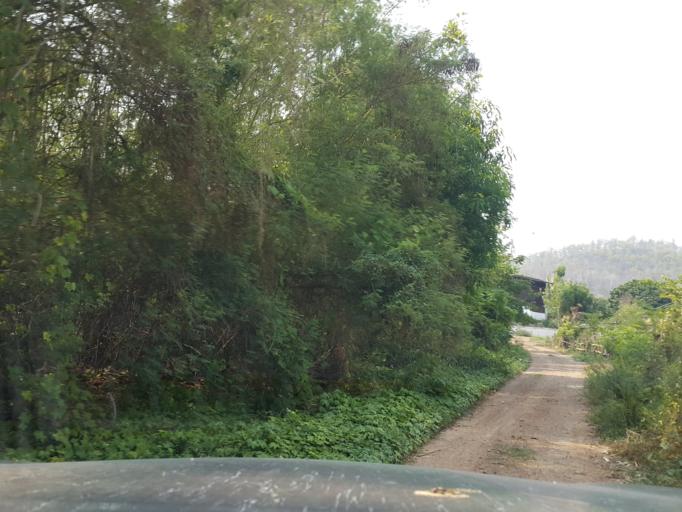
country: TH
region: Lampang
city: Mae Phrik
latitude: 17.5280
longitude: 98.9916
